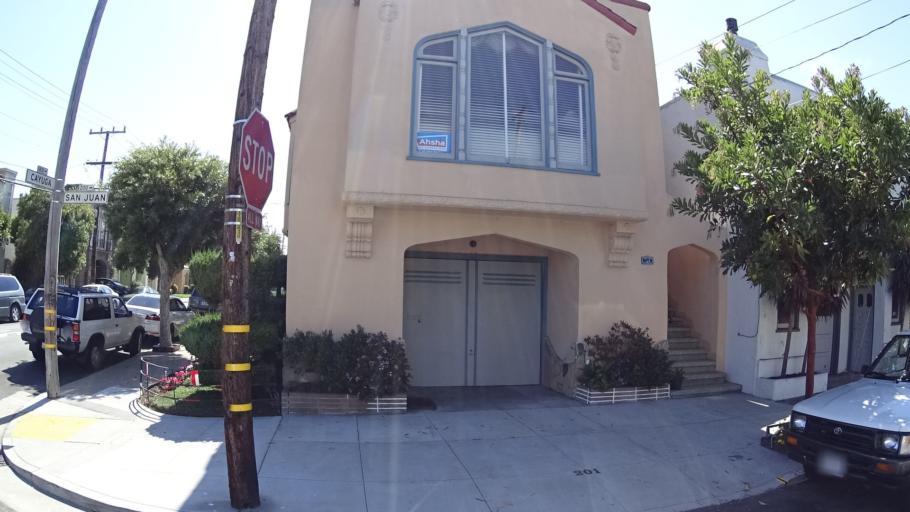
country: US
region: California
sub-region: San Mateo County
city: Daly City
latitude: 37.7251
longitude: -122.4380
